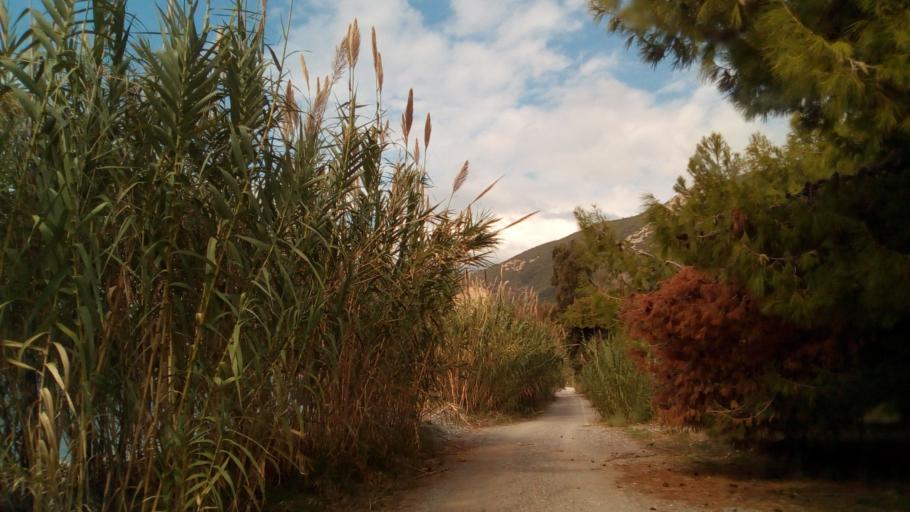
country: GR
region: West Greece
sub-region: Nomos Achaias
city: Kamarai
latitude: 38.3931
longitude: 21.9985
